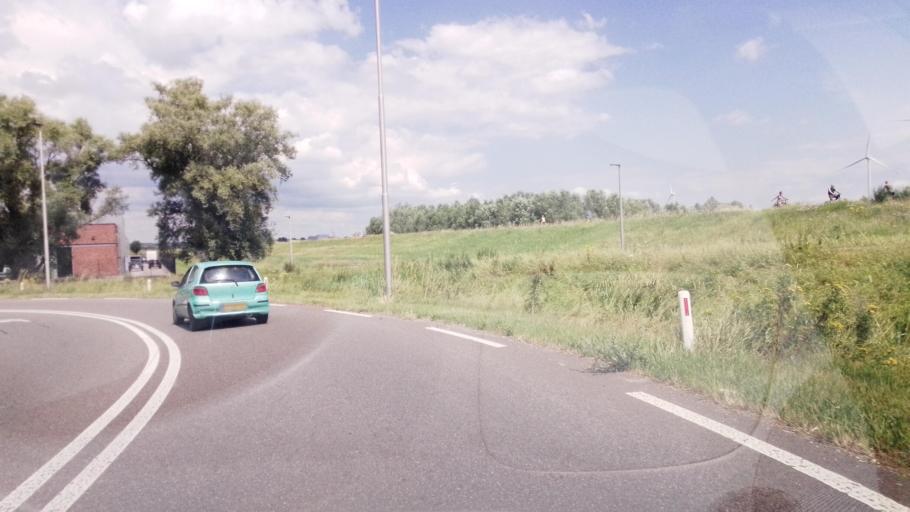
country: NL
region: Gelderland
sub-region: Gemeente Arnhem
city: Arnhem
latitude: 51.9575
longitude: 5.9305
